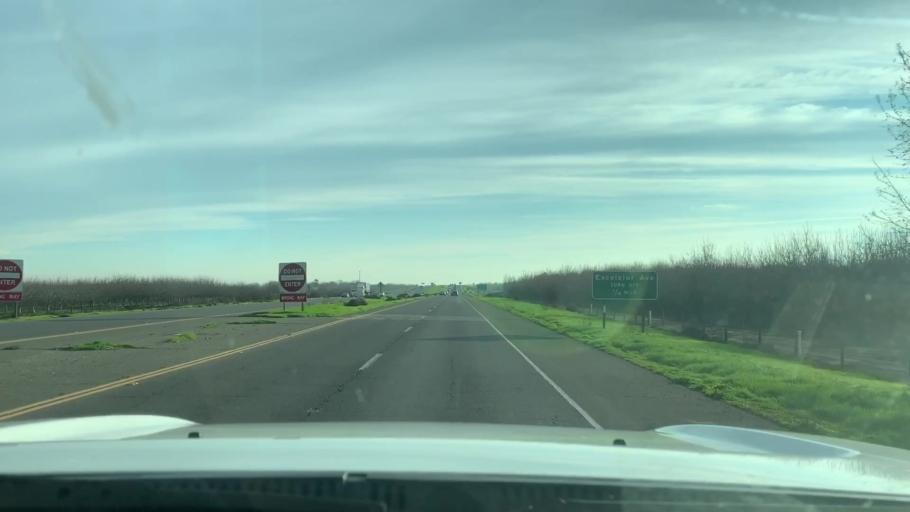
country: US
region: California
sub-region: Fresno County
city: Riverdale
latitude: 36.4086
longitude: -119.8058
